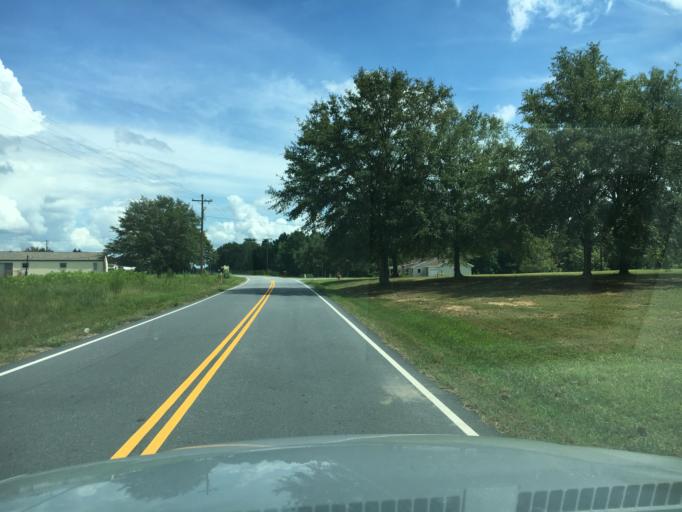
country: US
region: South Carolina
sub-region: Anderson County
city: Honea Path
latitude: 34.5160
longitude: -82.4187
